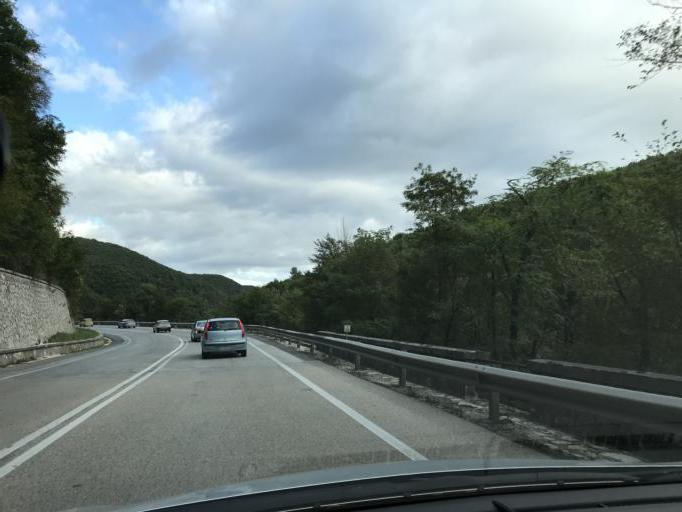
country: IT
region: Umbria
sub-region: Provincia di Perugia
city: Spoleto
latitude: 42.6873
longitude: 12.7249
